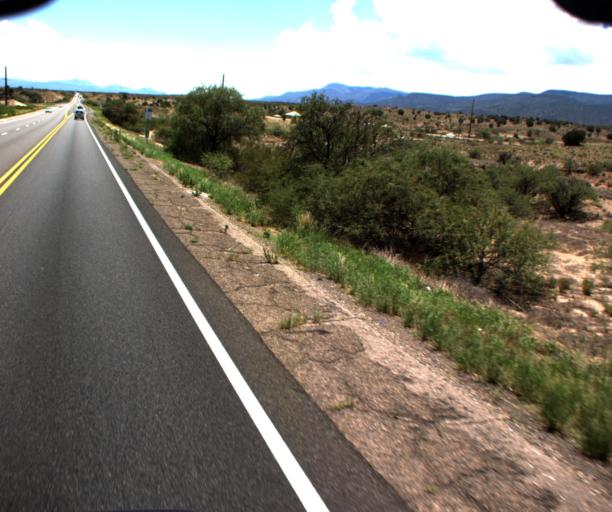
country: US
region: Arizona
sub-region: Yavapai County
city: Cornville
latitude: 34.6403
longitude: -111.9461
